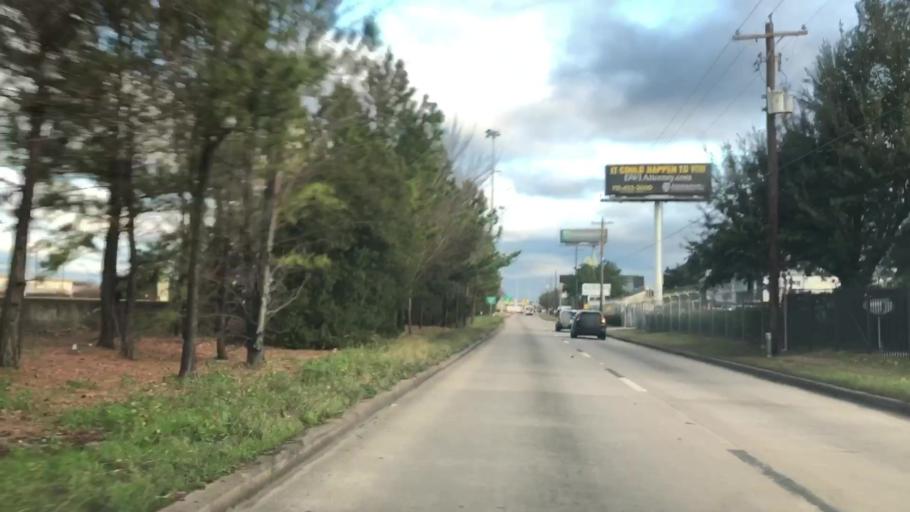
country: US
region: Texas
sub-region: Harris County
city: Aldine
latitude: 29.9116
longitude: -95.4121
